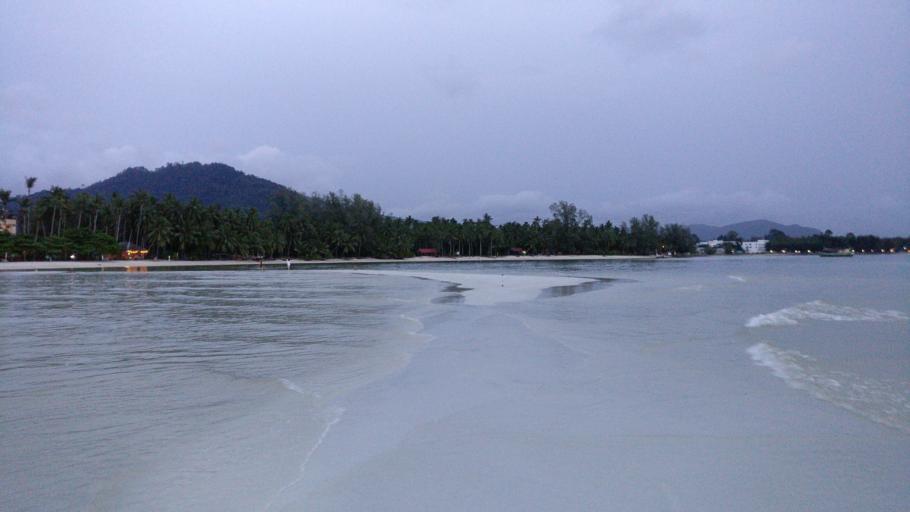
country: TH
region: Surat Thani
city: Ko Samui
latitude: 9.5304
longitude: 99.9327
